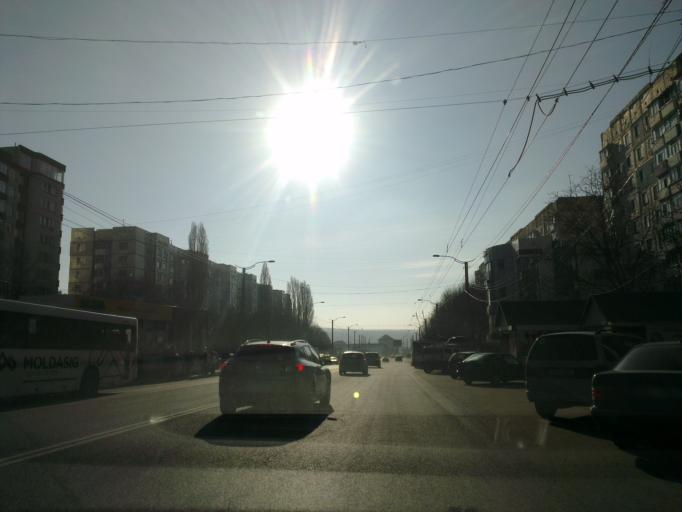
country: MD
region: Chisinau
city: Chisinau
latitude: 47.0385
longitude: 28.8841
